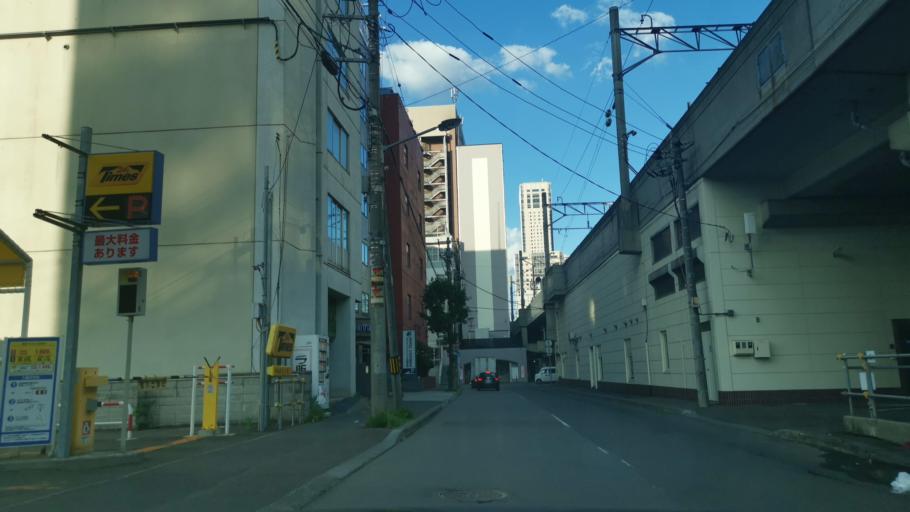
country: JP
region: Hokkaido
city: Sapporo
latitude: 43.0674
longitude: 141.3445
